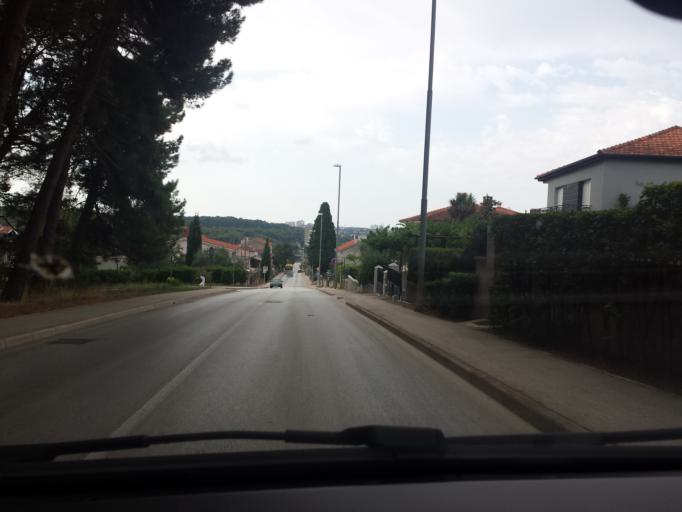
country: HR
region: Istarska
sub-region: Grad Pula
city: Pula
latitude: 44.8930
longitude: 13.8504
